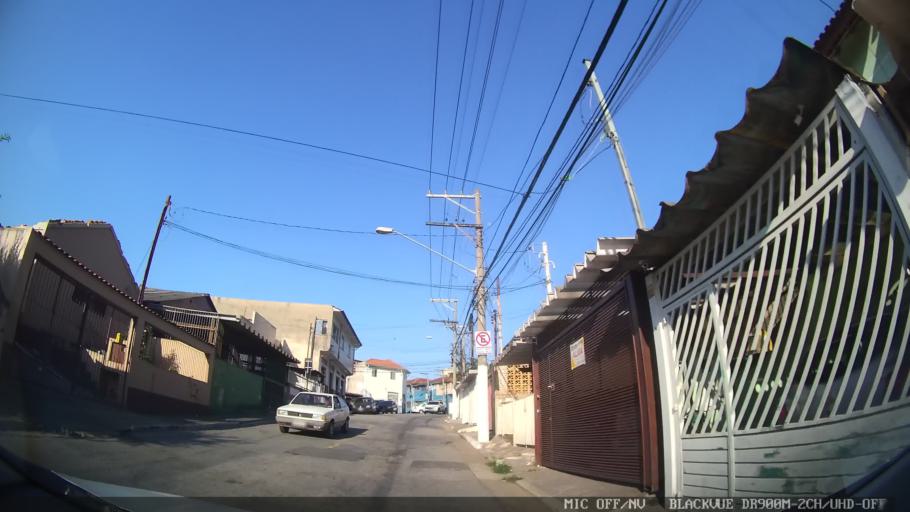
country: BR
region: Sao Paulo
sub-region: Sao Paulo
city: Sao Paulo
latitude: -23.4905
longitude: -46.6534
